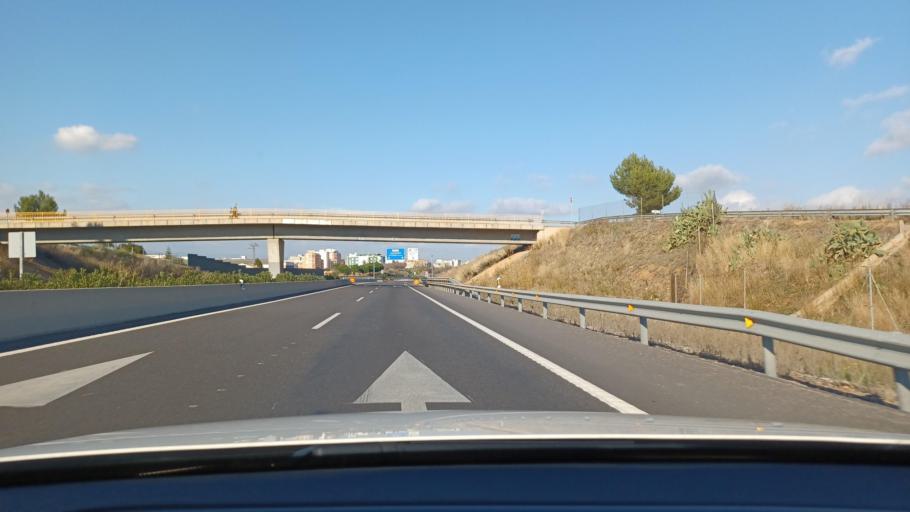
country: ES
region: Valencia
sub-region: Provincia de Castello
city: Betxi
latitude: 39.9174
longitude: -0.1957
